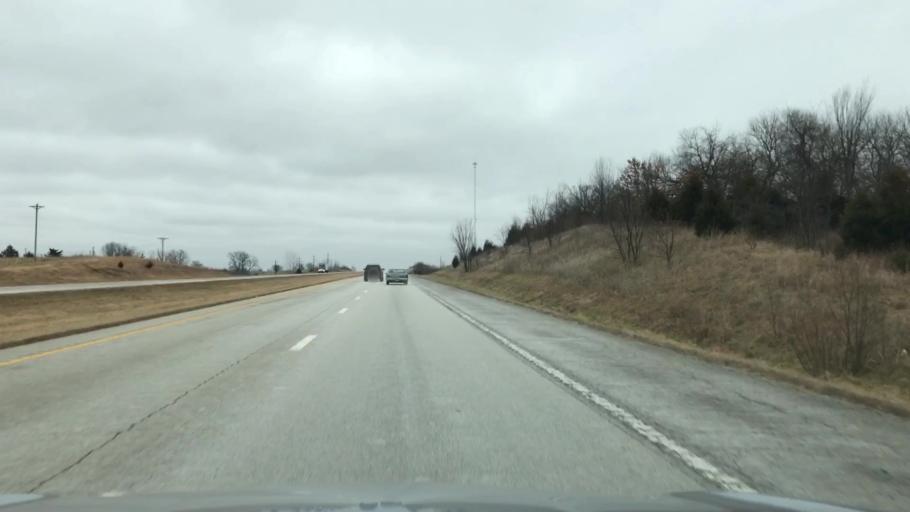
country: US
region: Missouri
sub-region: Clinton County
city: Cameron
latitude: 39.7525
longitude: -94.1967
